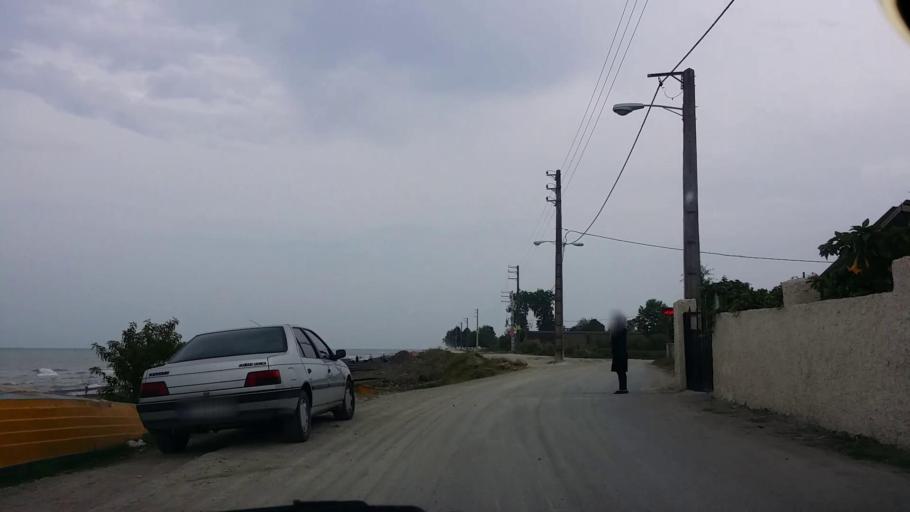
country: IR
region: Mazandaran
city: Chalus
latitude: 36.6857
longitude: 51.4196
